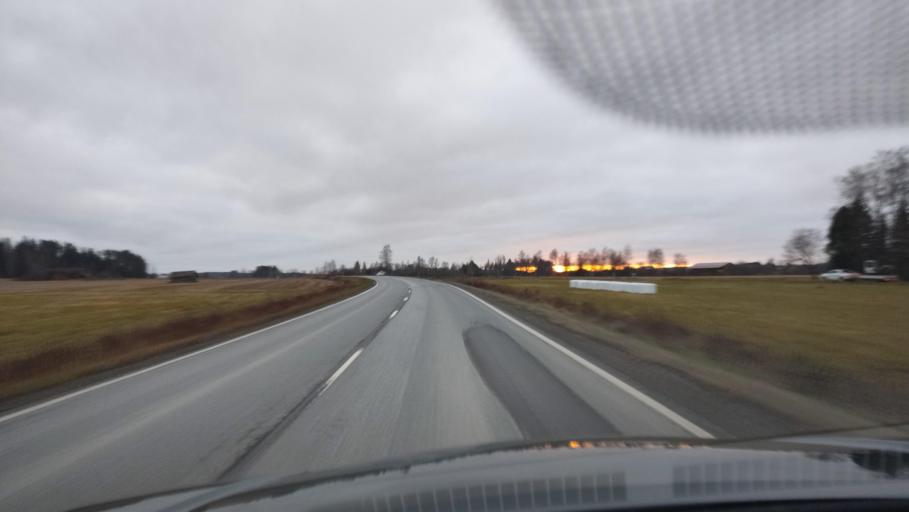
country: FI
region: Southern Ostrobothnia
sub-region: Suupohja
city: Kauhajoki
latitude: 62.3763
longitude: 22.0847
